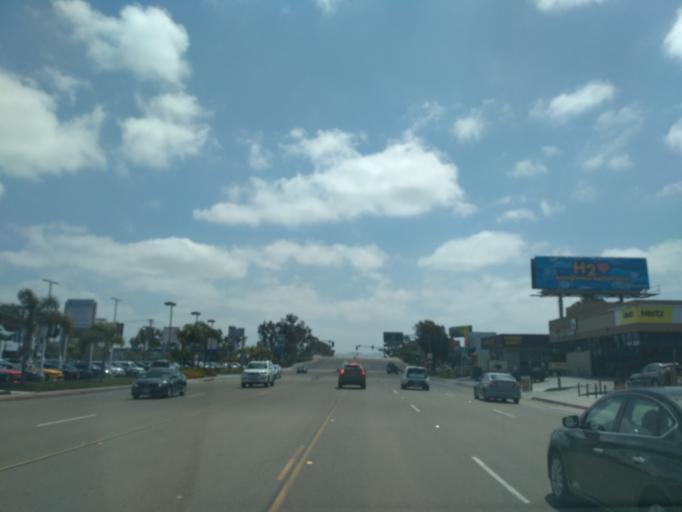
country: US
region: California
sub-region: San Diego County
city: San Diego
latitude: 32.8218
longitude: -117.1509
